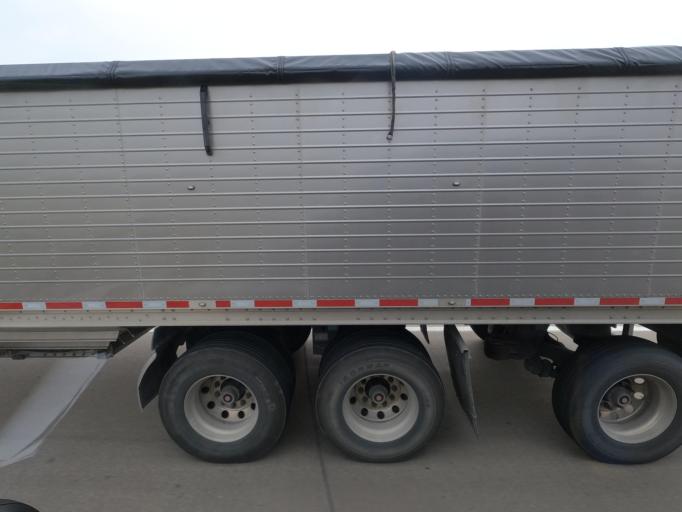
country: US
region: Iowa
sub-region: Marion County
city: Pella
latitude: 41.3892
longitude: -92.9166
